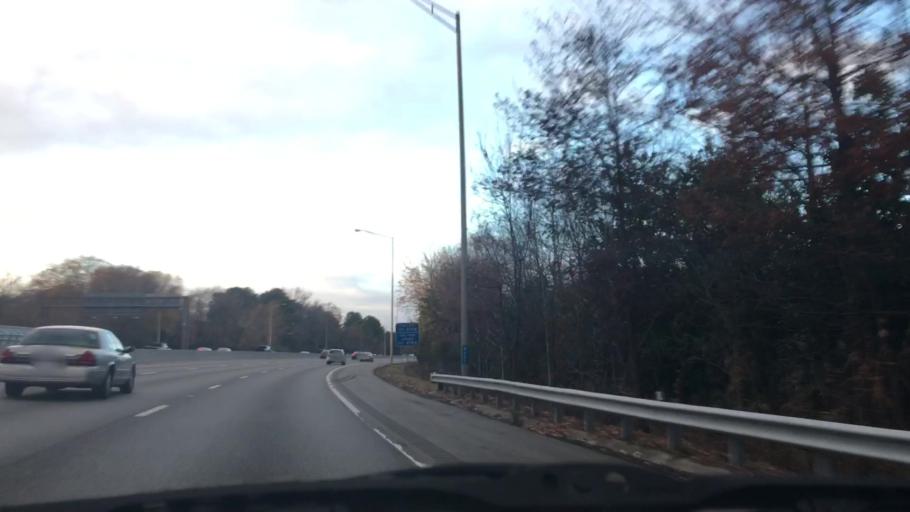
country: US
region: Virginia
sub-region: City of Norfolk
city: Norfolk
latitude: 36.8865
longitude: -76.2272
